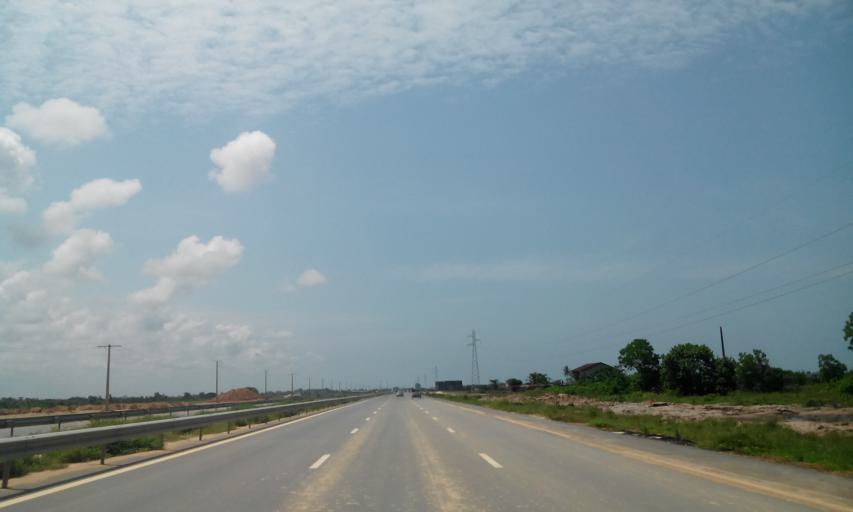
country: CI
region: Sud-Comoe
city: Grand-Bassam
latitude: 5.2306
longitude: -3.7556
